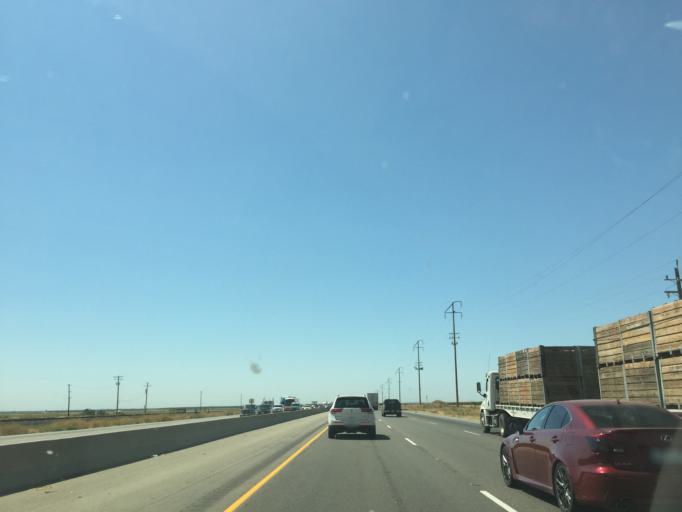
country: US
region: California
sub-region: Kern County
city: Greenacres
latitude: 35.4579
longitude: -119.1088
